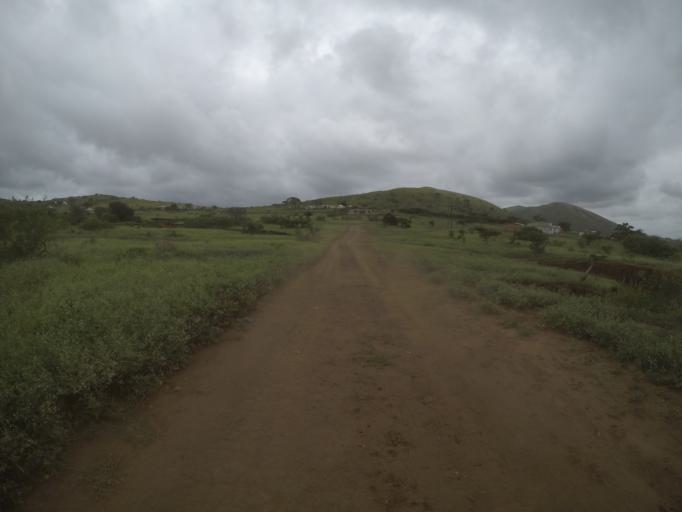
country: ZA
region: KwaZulu-Natal
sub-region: uThungulu District Municipality
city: Empangeni
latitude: -28.6024
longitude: 31.8642
